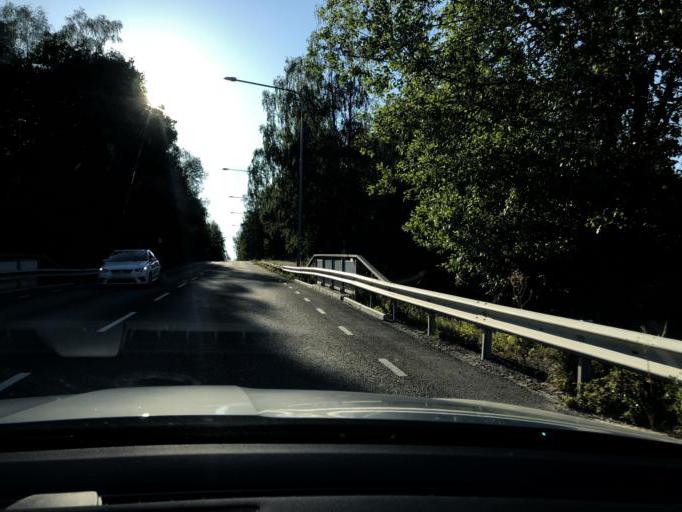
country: SE
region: Stockholm
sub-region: Sodertalje Kommun
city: Soedertaelje
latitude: 59.1827
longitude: 17.6062
